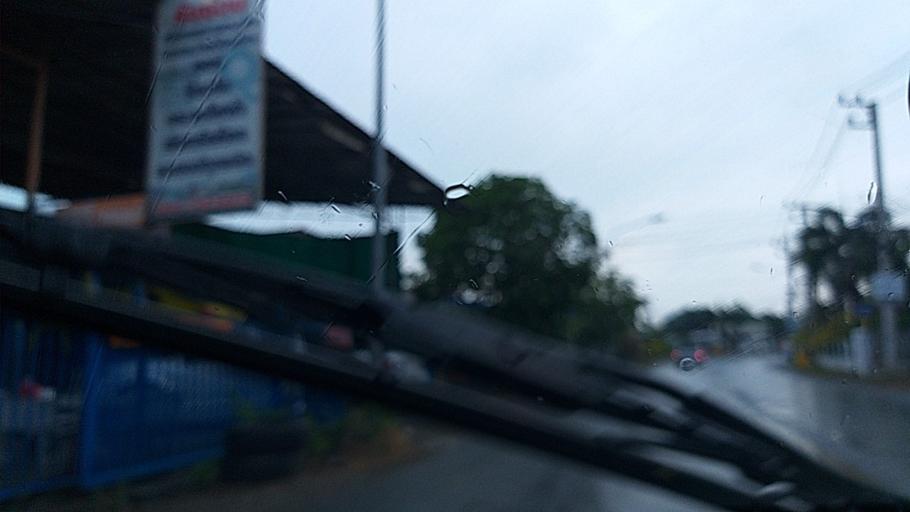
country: TH
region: Phra Nakhon Si Ayutthaya
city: Phra Nakhon Si Ayutthaya
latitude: 14.3399
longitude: 100.5414
